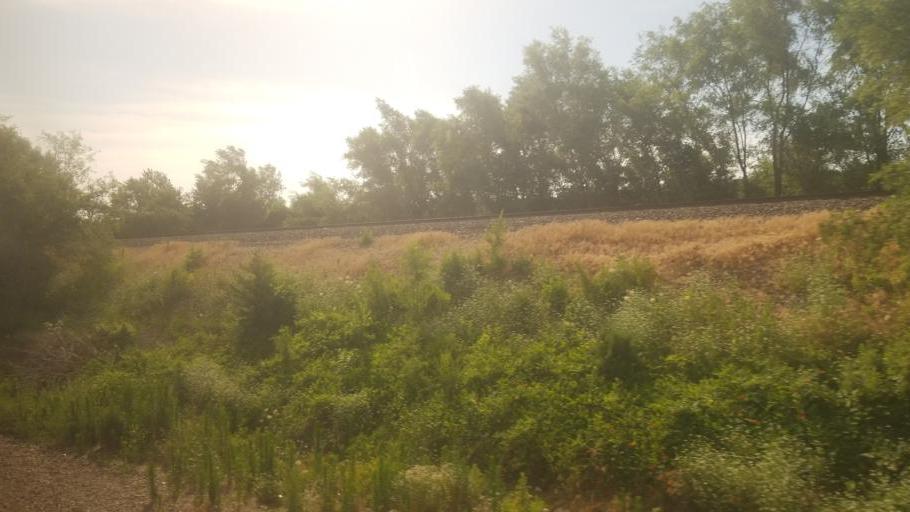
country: US
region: Kansas
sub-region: Johnson County
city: Shawnee
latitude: 39.0615
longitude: -94.7520
